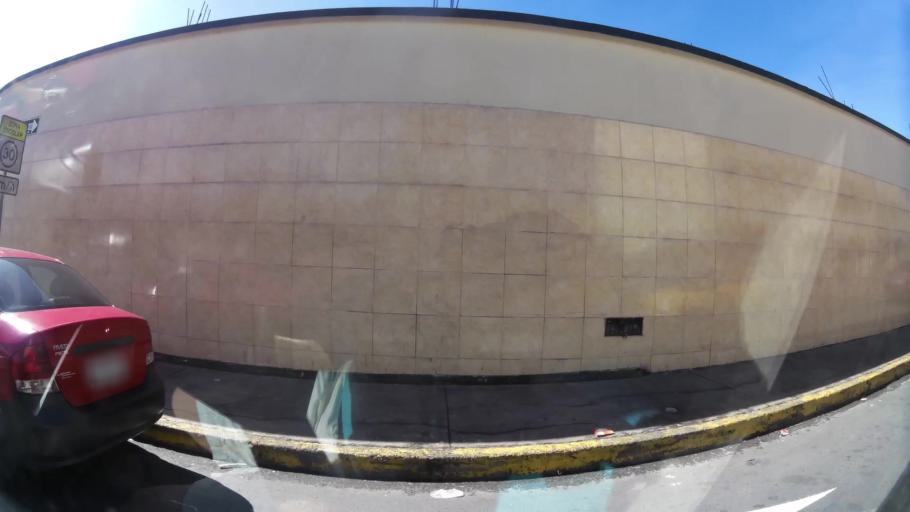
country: EC
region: Pichincha
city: Quito
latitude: -0.2805
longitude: -78.5567
